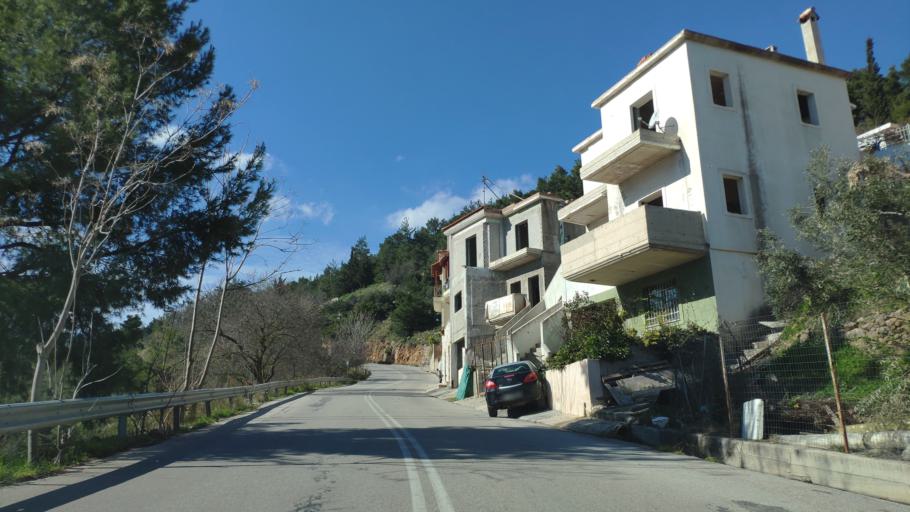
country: GR
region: Attica
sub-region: Nomarchia Anatolikis Attikis
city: Afidnes
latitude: 38.2041
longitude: 23.8342
